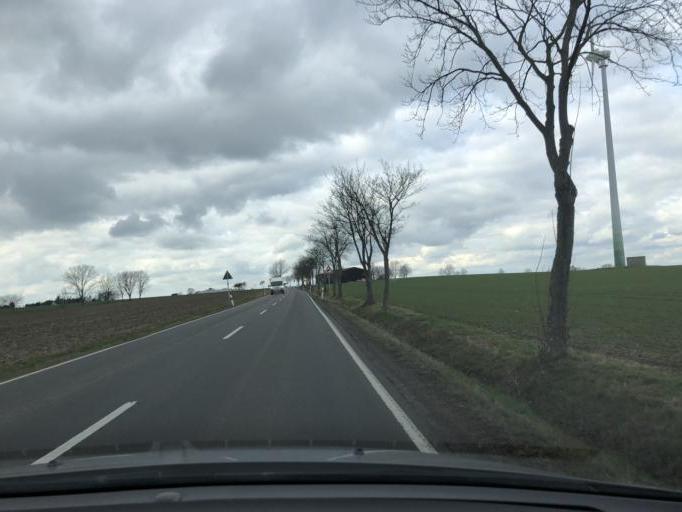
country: DE
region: Saxony
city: Grossweitzschen
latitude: 51.1519
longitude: 13.0736
